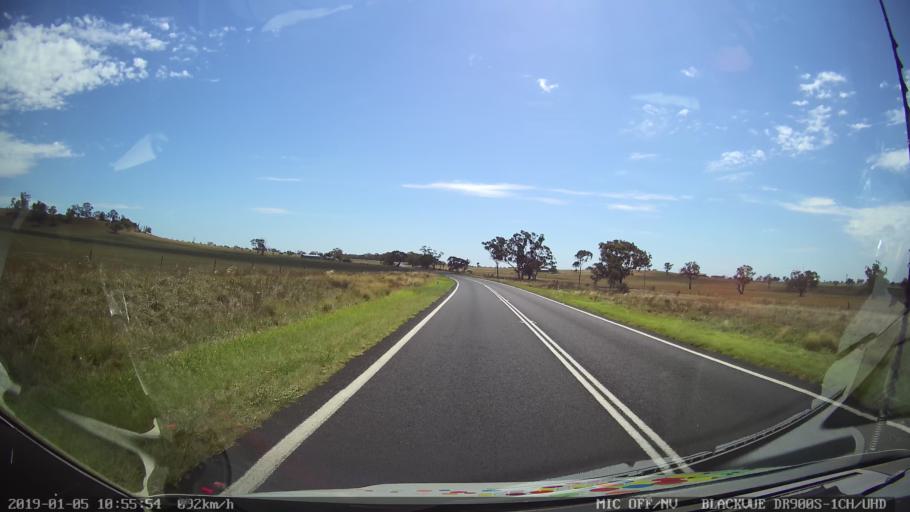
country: AU
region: New South Wales
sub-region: Warrumbungle Shire
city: Coonabarabran
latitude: -31.4461
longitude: 149.1502
